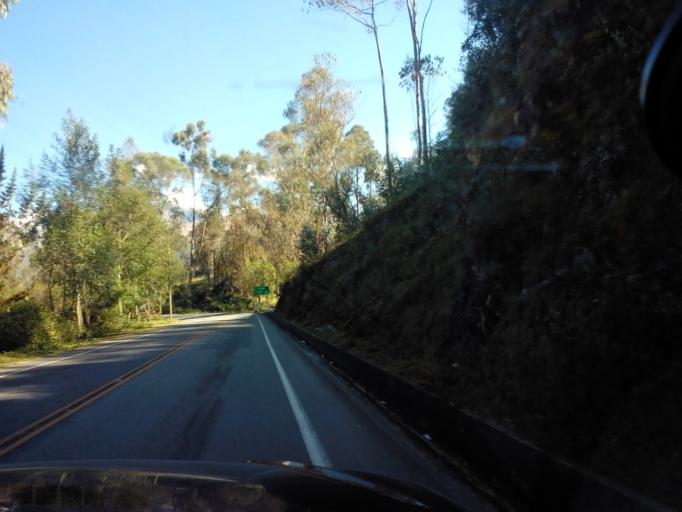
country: PE
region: Apurimac
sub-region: Provincia de Abancay
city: Tamburco
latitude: -13.5951
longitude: -72.8397
